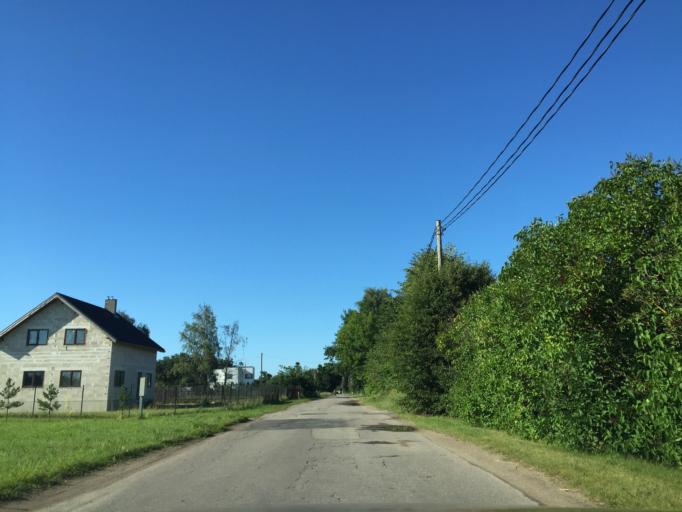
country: LV
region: Riga
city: Jaunciems
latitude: 57.0554
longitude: 24.1379
